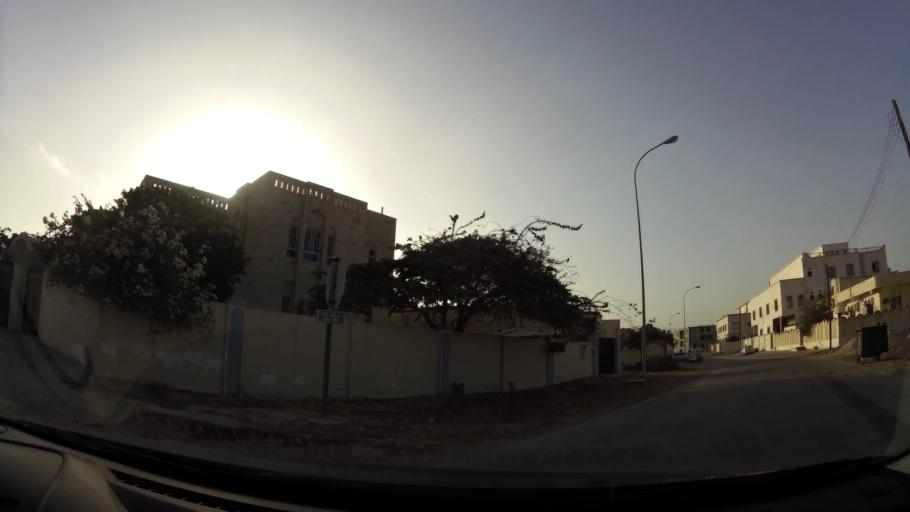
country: OM
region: Zufar
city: Salalah
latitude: 16.9997
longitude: 54.0251
